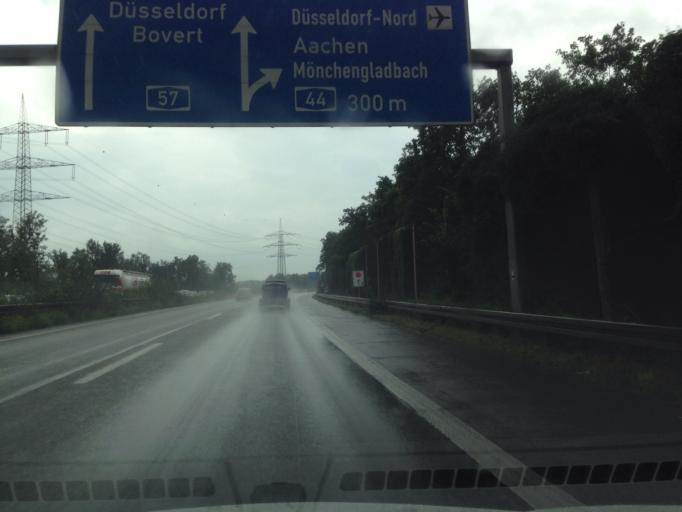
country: DE
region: North Rhine-Westphalia
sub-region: Regierungsbezirk Dusseldorf
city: Meerbusch
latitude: 51.3019
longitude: 6.6370
